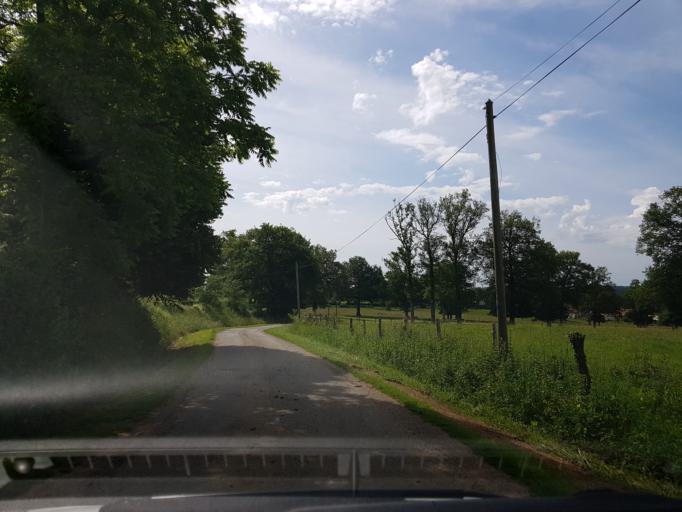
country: FR
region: Poitou-Charentes
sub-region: Departement de la Charente
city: Etagnac
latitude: 45.9565
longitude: 0.7819
